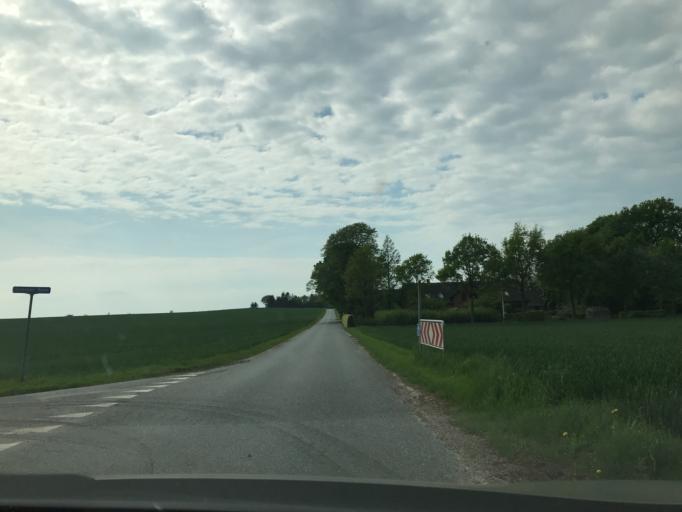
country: DK
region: South Denmark
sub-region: Middelfart Kommune
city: Ejby
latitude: 55.3550
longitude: 9.8929
